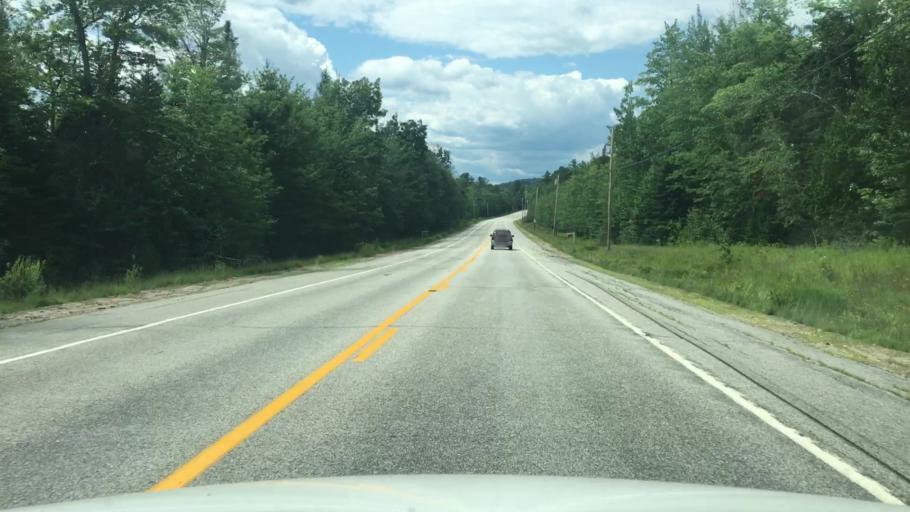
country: US
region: Maine
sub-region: Oxford County
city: West Paris
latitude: 44.3699
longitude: -70.6014
